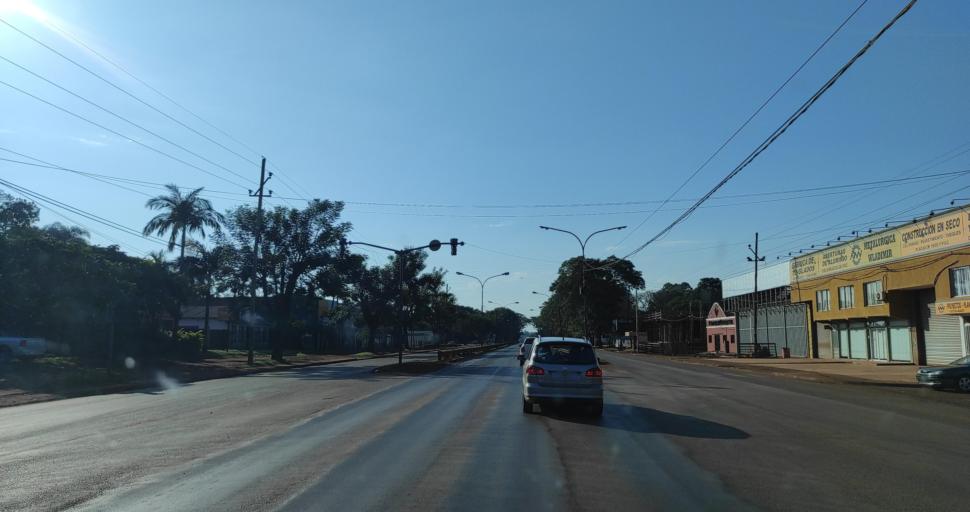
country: AR
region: Corrientes
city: Gobernador Ingeniero Valentin Virasoro
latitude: -28.0433
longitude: -56.0129
